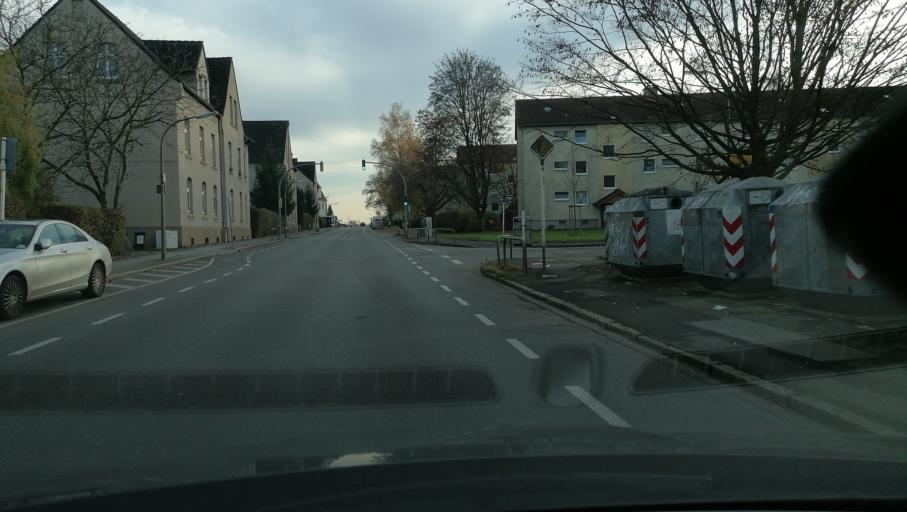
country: DE
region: North Rhine-Westphalia
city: Waltrop
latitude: 51.5587
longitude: 7.3808
